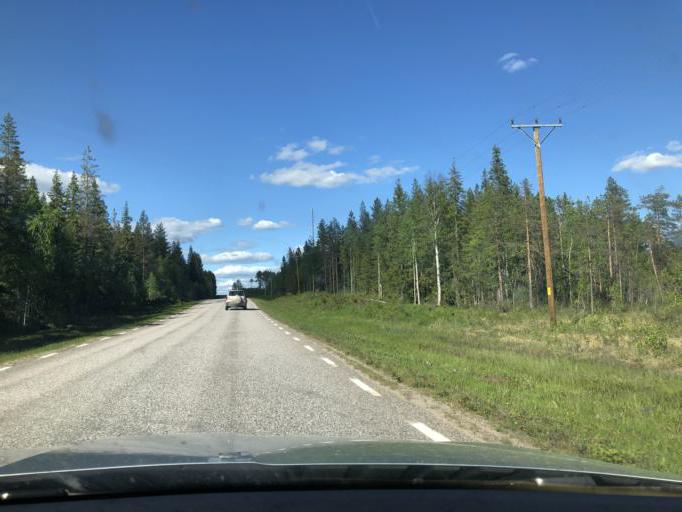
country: SE
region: Norrbotten
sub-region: Kalix Kommun
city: Kalix
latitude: 66.0364
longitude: 23.1729
